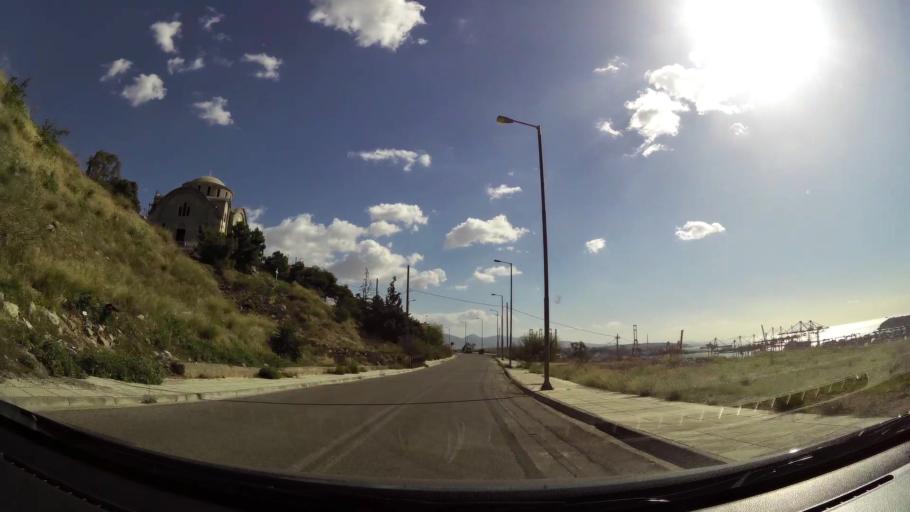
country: GR
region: Attica
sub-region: Nomos Piraios
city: Perama
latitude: 37.9645
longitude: 23.5885
